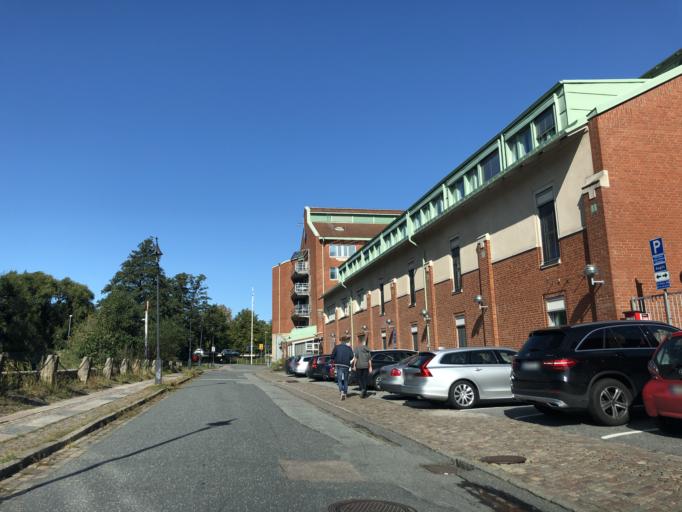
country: SE
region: Vaestra Goetaland
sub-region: Goteborg
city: Goeteborg
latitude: 57.7059
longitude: 11.9902
